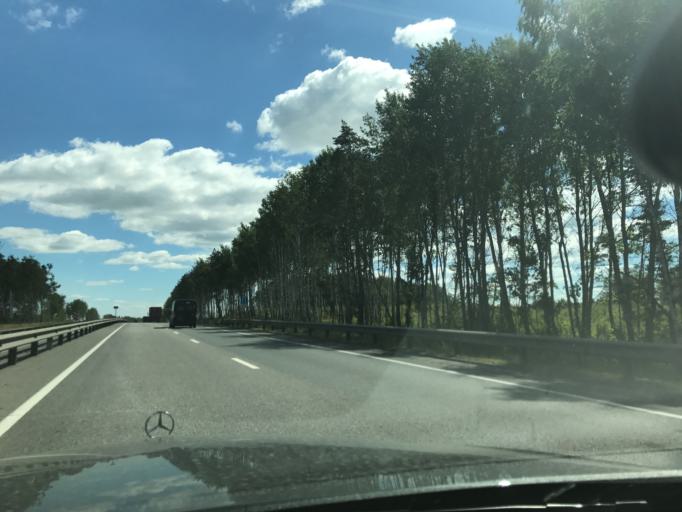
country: RU
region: Vladimir
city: Novovyazniki
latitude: 56.1974
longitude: 42.3678
